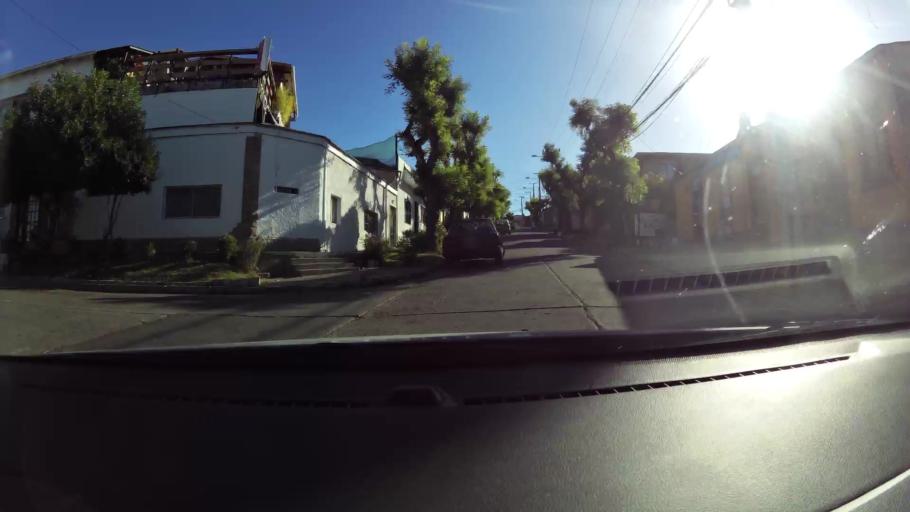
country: CL
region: Valparaiso
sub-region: Provincia de Valparaiso
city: Vina del Mar
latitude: -33.0311
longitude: -71.5659
